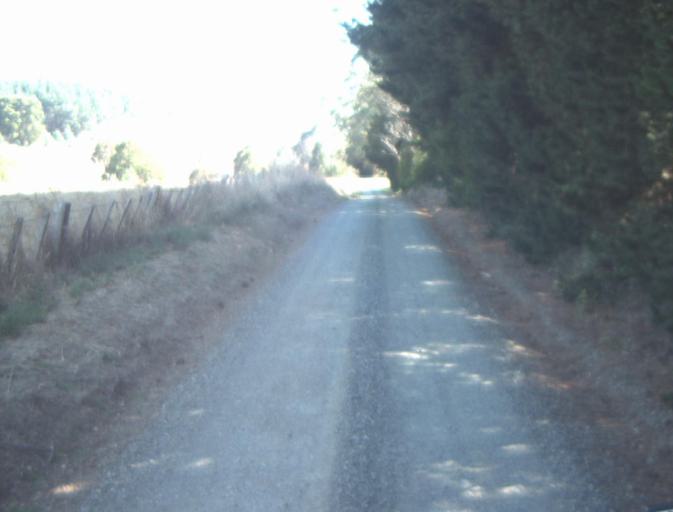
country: AU
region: Tasmania
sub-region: Launceston
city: Mayfield
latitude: -41.1725
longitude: 147.2125
